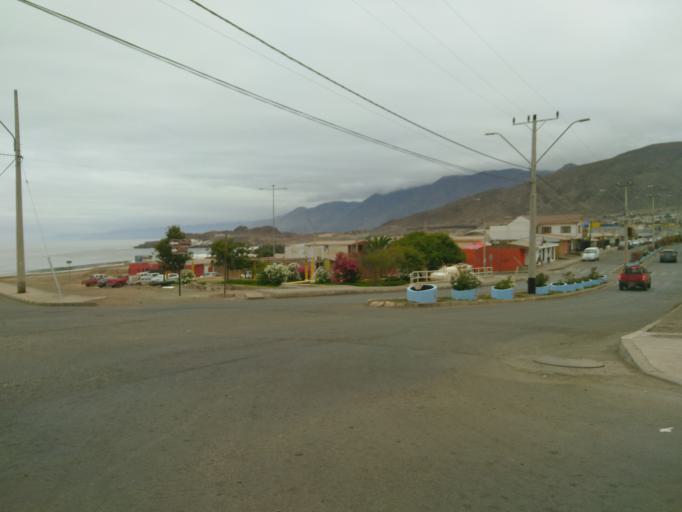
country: CL
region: Antofagasta
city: Taltal
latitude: -25.4037
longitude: -70.4790
